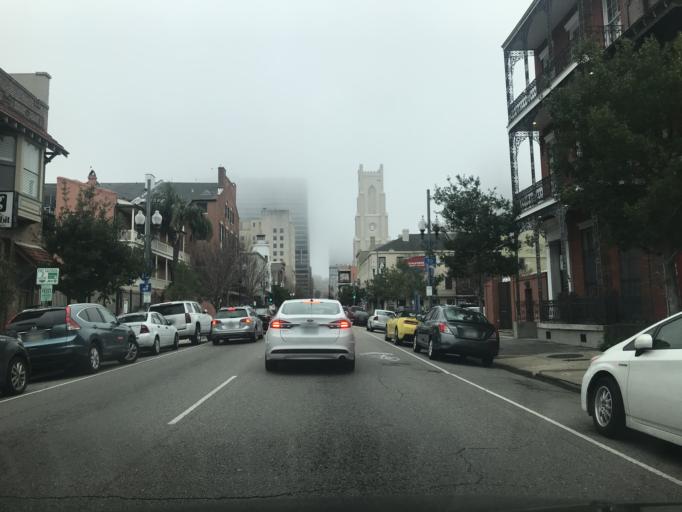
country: US
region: Louisiana
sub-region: Orleans Parish
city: New Orleans
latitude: 29.9449
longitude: -90.0706
